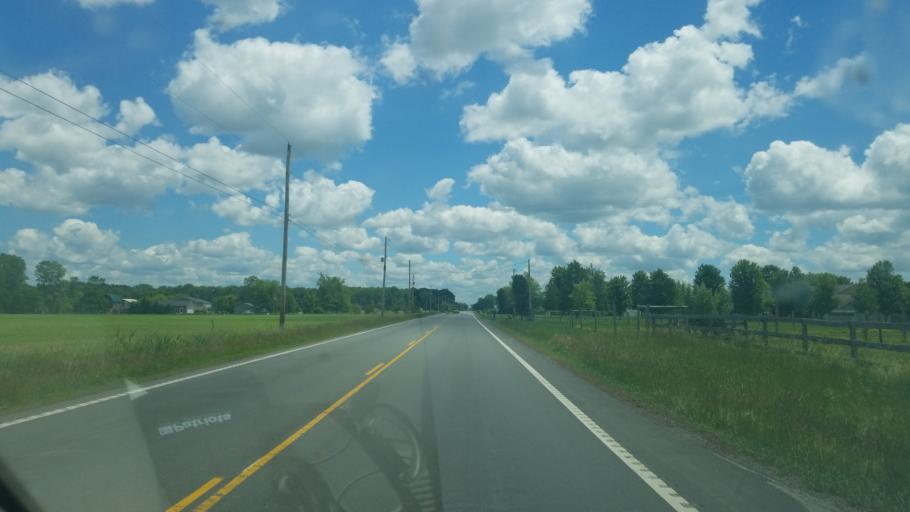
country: US
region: Ohio
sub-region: Huron County
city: New London
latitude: 41.0295
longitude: -82.3379
